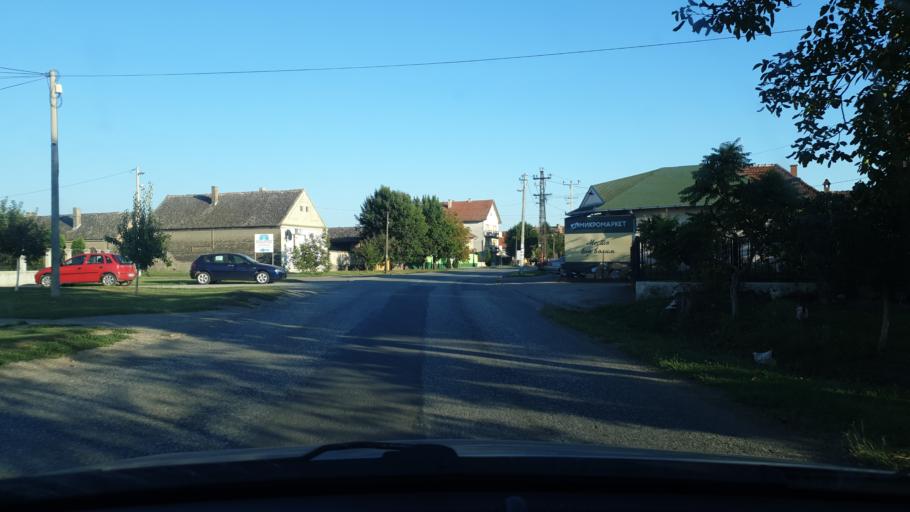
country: RS
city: Putinci
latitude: 44.9599
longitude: 19.9236
